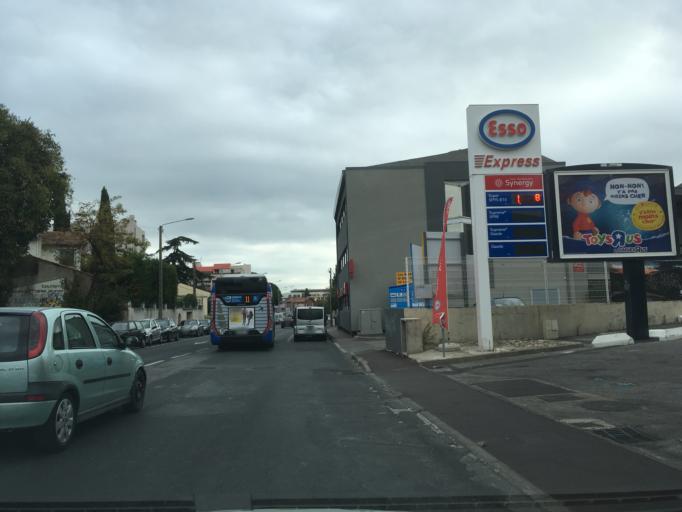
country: FR
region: Languedoc-Roussillon
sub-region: Departement de l'Herault
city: Montpellier
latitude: 43.5947
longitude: 3.8885
